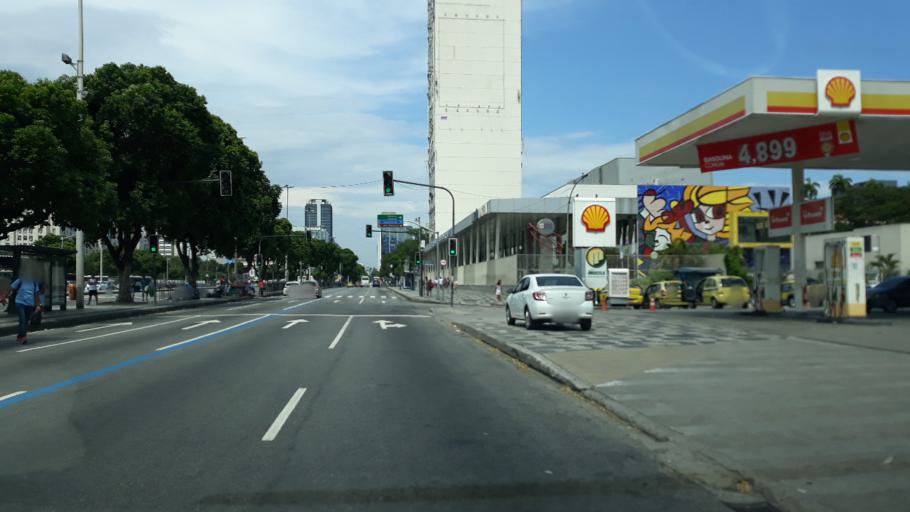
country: BR
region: Rio de Janeiro
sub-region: Rio De Janeiro
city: Rio de Janeiro
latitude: -22.9061
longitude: -43.1932
